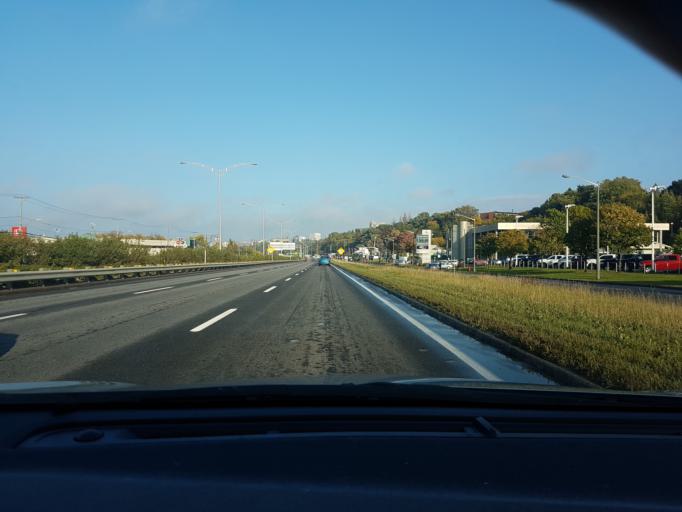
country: CA
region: Quebec
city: Quebec
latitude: 46.7955
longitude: -71.2723
